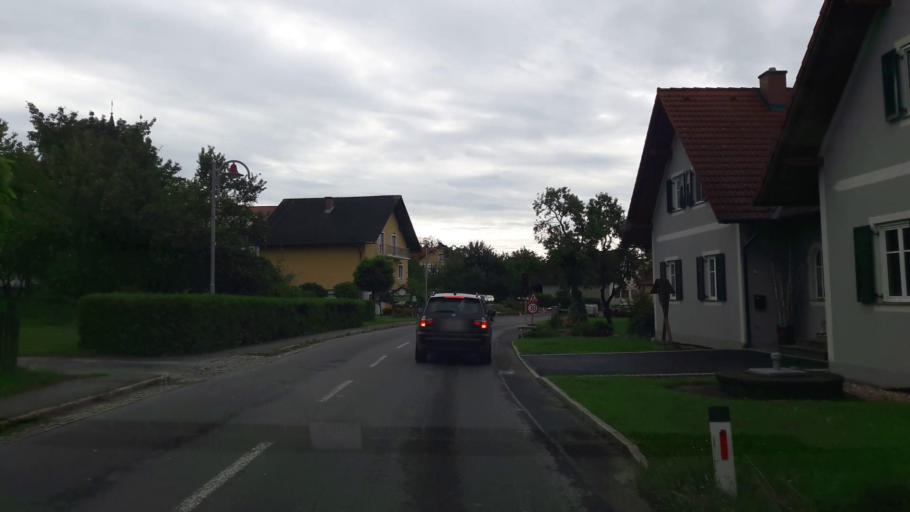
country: AT
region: Styria
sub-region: Politischer Bezirk Hartberg-Fuerstenfeld
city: Ebersdorf
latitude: 47.2011
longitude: 15.9575
